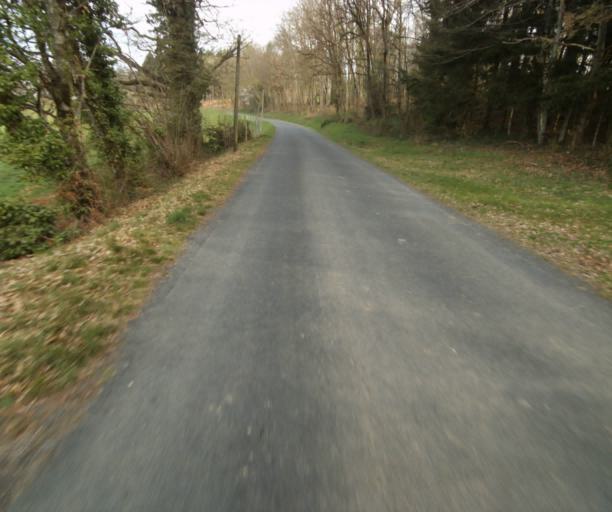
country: FR
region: Limousin
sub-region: Departement de la Correze
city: Chamboulive
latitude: 45.4504
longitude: 1.7501
